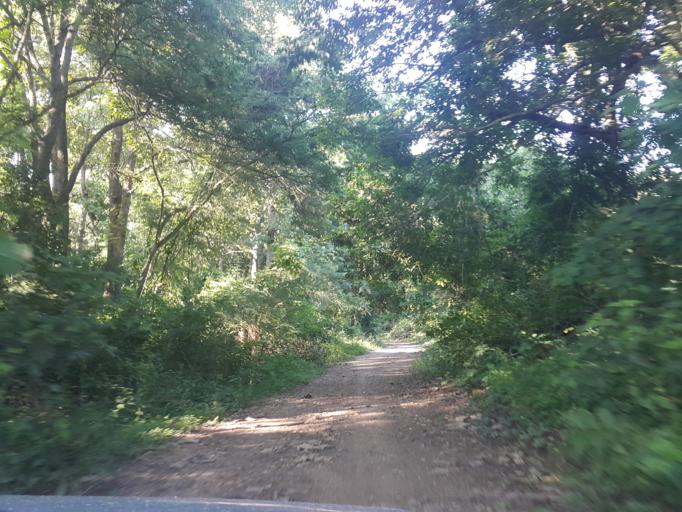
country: TH
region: Chiang Mai
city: Mae On
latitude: 18.7066
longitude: 99.2031
